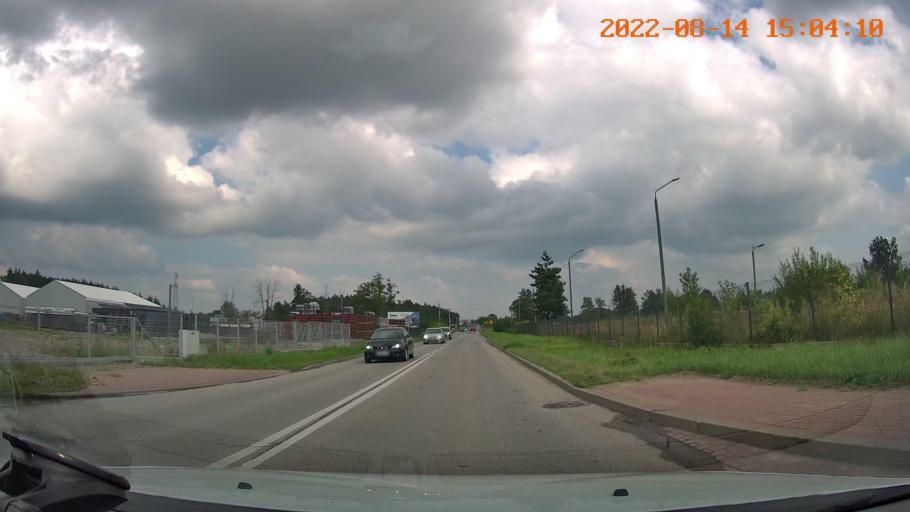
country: PL
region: Swietokrzyskie
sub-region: Powiat kielecki
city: Kostomloty Drugie
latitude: 50.8823
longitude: 20.5443
